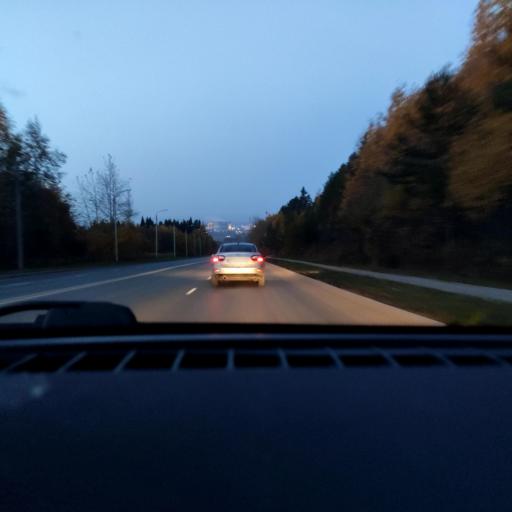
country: RU
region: Perm
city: Kondratovo
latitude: 57.9474
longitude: 56.1750
